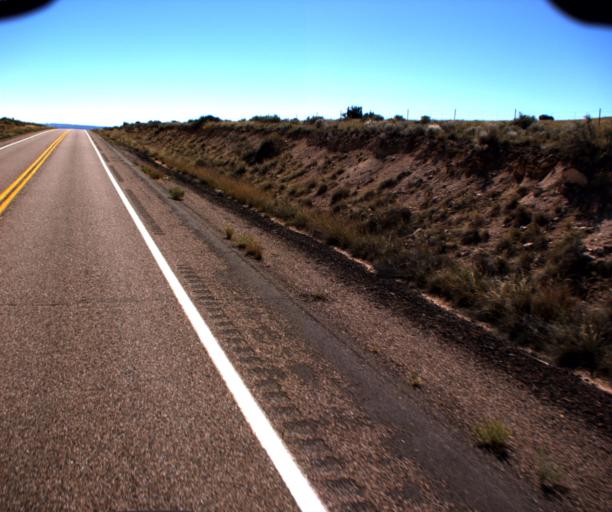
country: US
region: Arizona
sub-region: Apache County
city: Saint Johns
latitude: 34.5609
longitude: -109.5022
